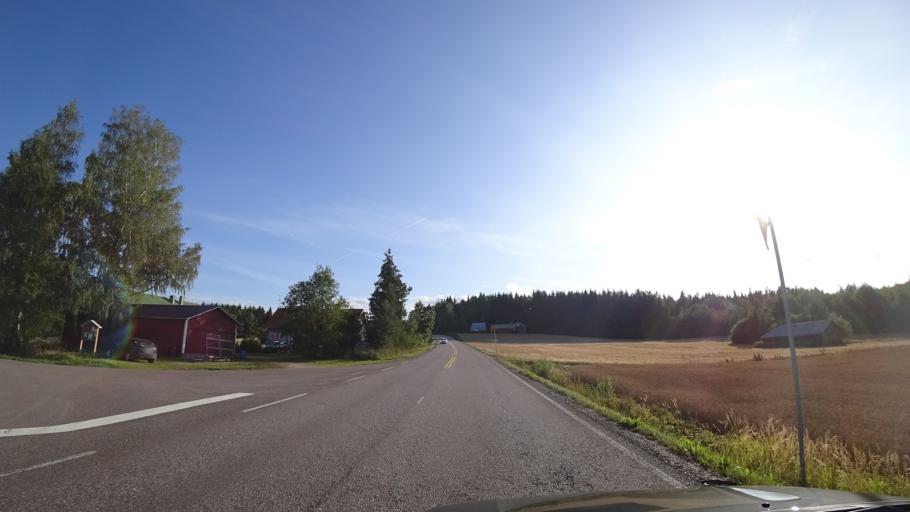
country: FI
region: Paijanne Tavastia
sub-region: Lahti
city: Asikkala
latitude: 61.1754
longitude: 25.3744
